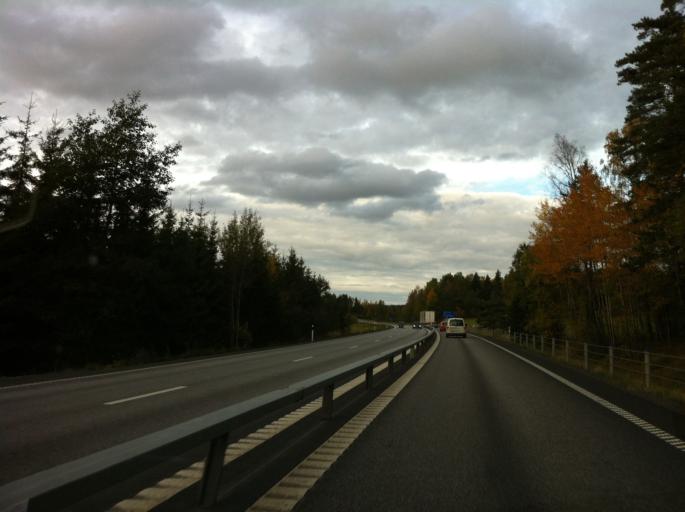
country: SE
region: OEstergoetland
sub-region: Motala Kommun
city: Ryd
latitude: 58.7700
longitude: 14.9939
